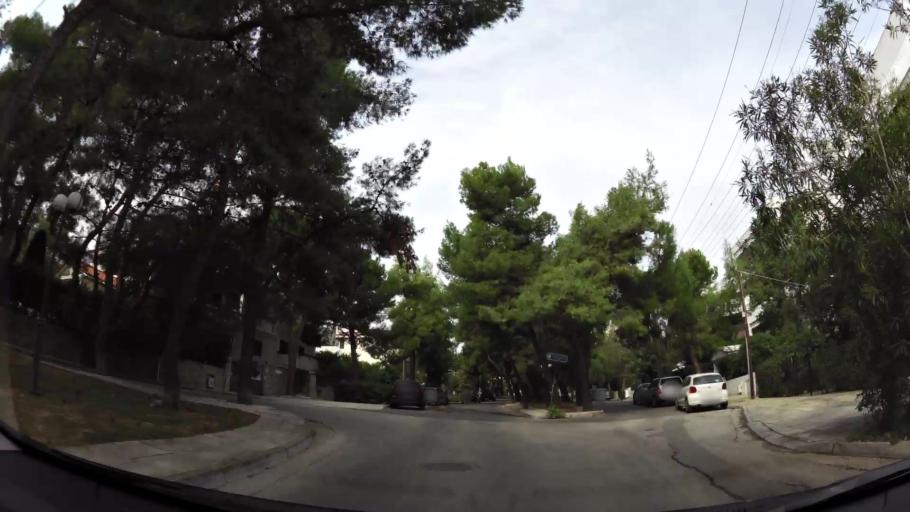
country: GR
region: Attica
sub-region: Nomarchia Athinas
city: Psychiko
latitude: 38.0172
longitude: 23.7666
